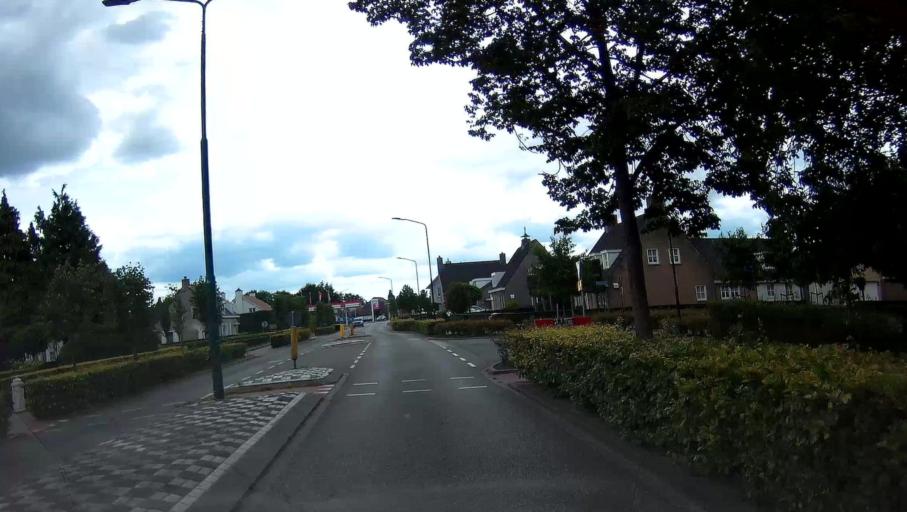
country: NL
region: North Brabant
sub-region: Gemeente Hilvarenbeek
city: Hilvarenbeek
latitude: 51.4937
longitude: 5.1346
